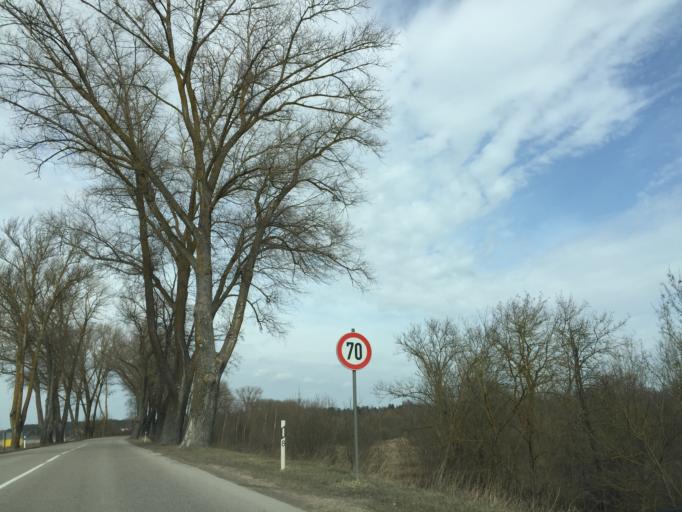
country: LV
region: Daugavpils
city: Daugavpils
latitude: 55.8897
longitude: 26.4738
